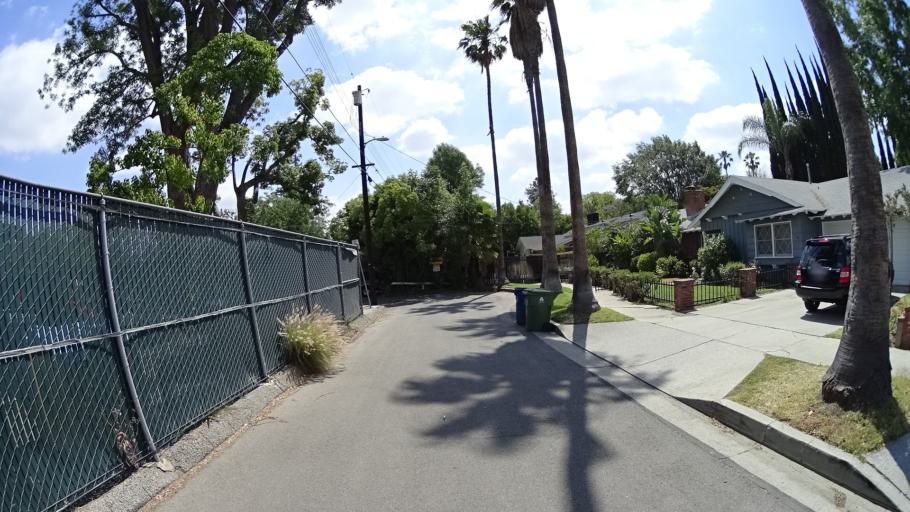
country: US
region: California
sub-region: Los Angeles County
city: Universal City
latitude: 34.1585
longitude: -118.3596
